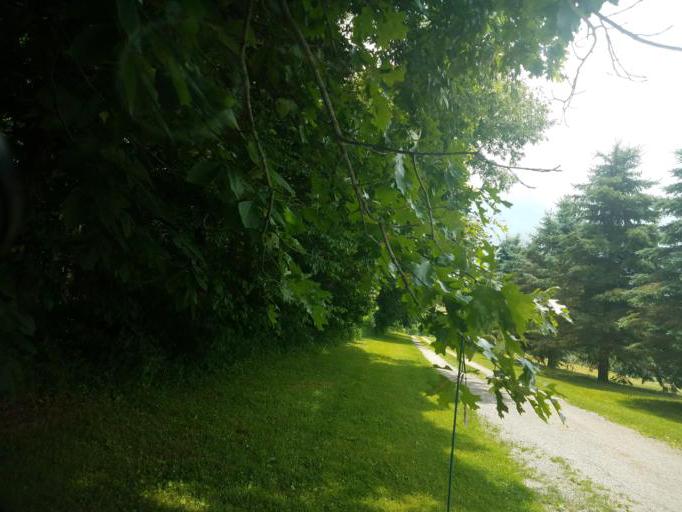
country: US
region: Ohio
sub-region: Sandusky County
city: Bellville
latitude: 40.5590
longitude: -82.4945
